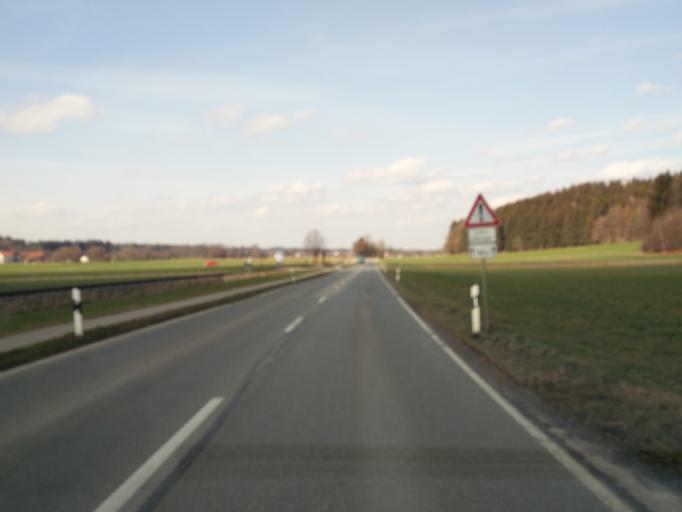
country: DE
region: Bavaria
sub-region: Upper Bavaria
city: Halfing
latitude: 47.9315
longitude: 12.2854
